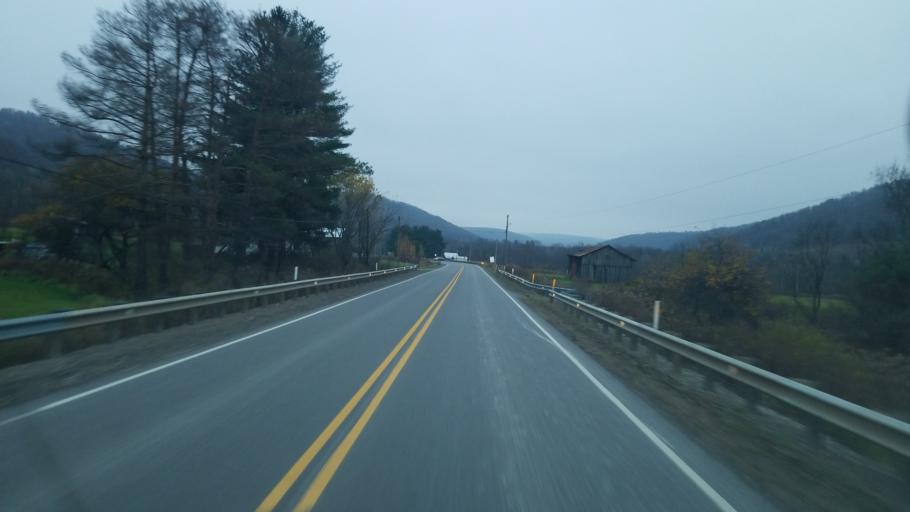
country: US
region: Pennsylvania
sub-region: McKean County
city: Smethport
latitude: 41.7835
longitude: -78.4125
